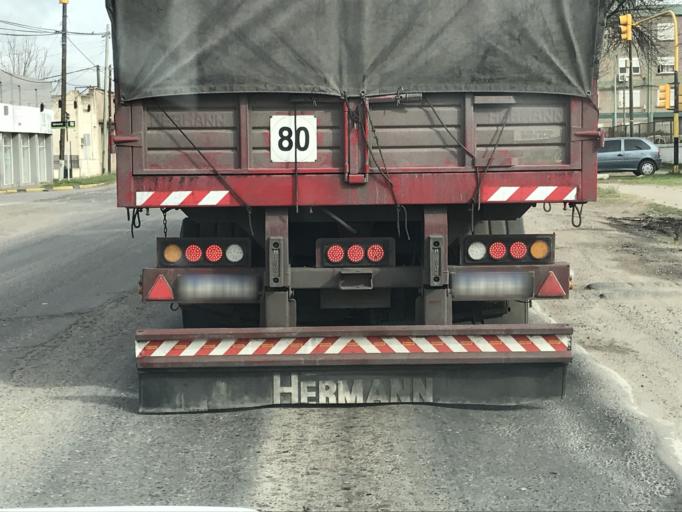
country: AR
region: Santa Fe
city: Canada de Gomez
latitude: -32.8102
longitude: -61.3953
